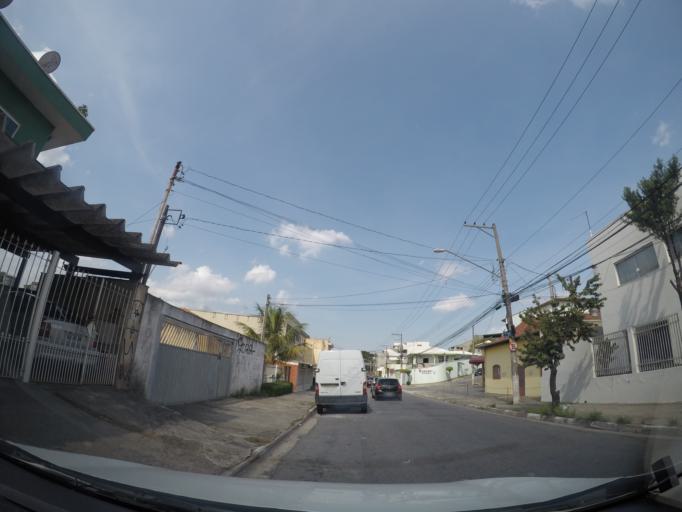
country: BR
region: Sao Paulo
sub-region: Guarulhos
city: Guarulhos
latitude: -23.4500
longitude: -46.4759
